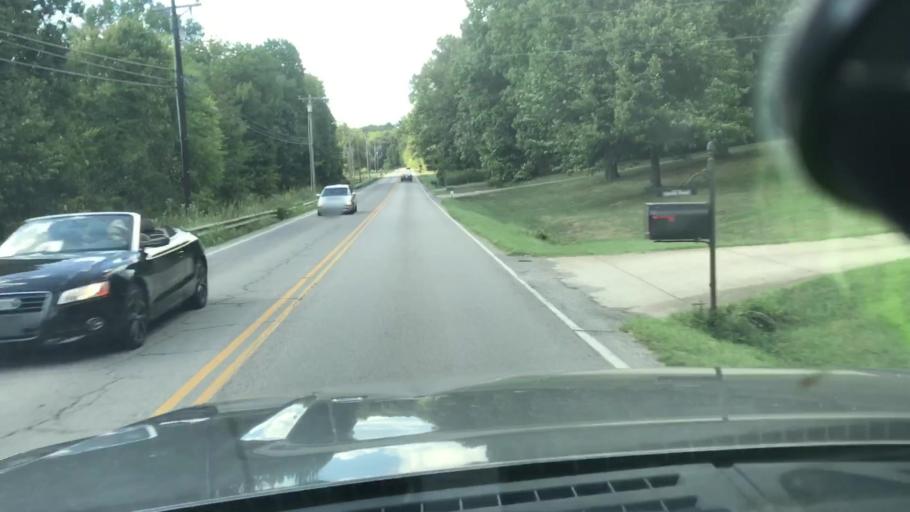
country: US
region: Tennessee
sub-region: Davidson County
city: Forest Hills
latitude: 36.0214
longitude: -86.8885
